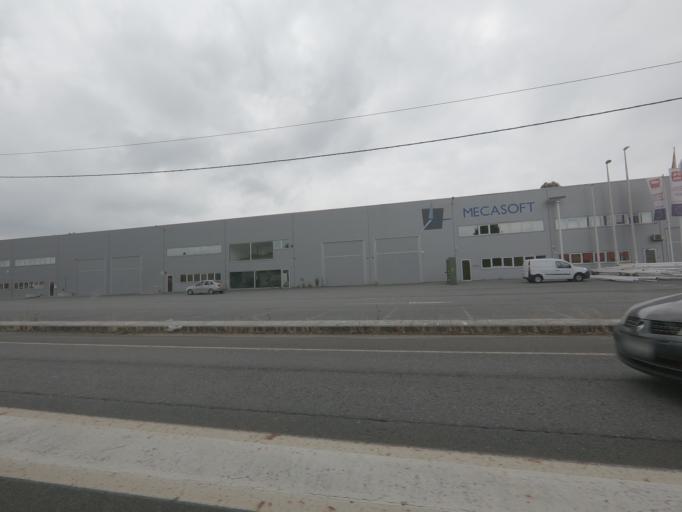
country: ES
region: Galicia
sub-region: Provincia de Pontevedra
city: Tomino
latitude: 41.9784
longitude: -8.7355
